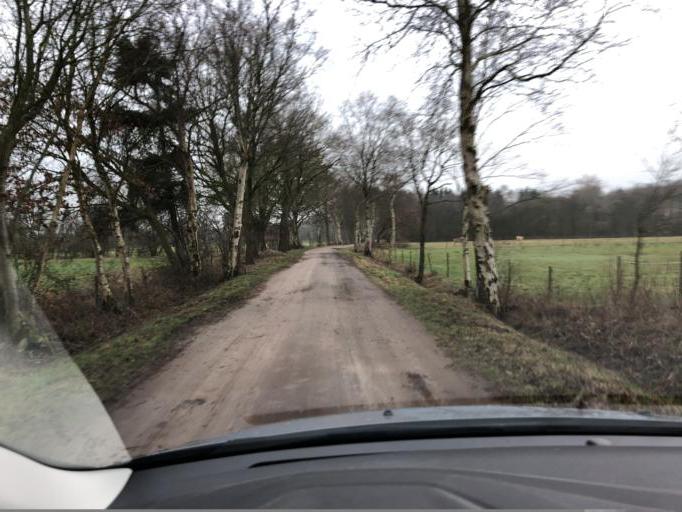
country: DE
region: Lower Saxony
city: Bad Zwischenahn
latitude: 53.1681
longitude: 8.0449
